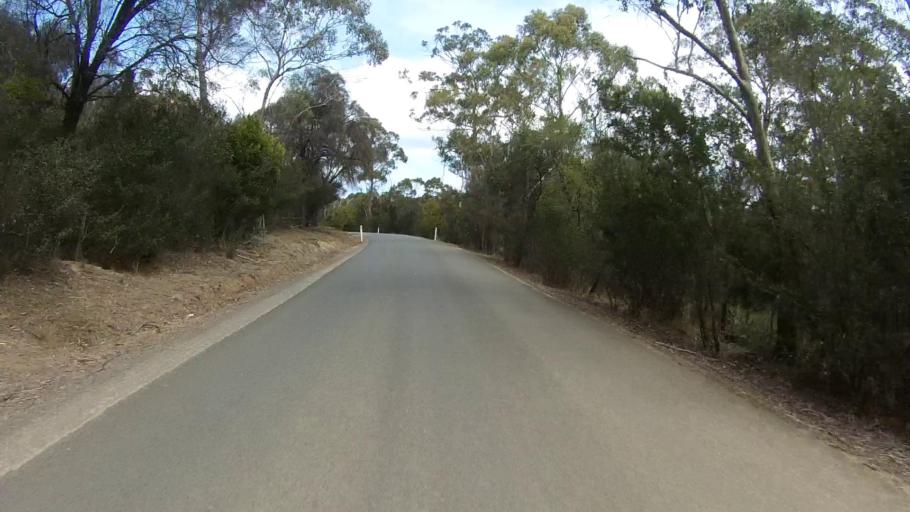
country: AU
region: Tasmania
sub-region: Kingborough
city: Blackmans Bay
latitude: -43.0357
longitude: 147.3057
